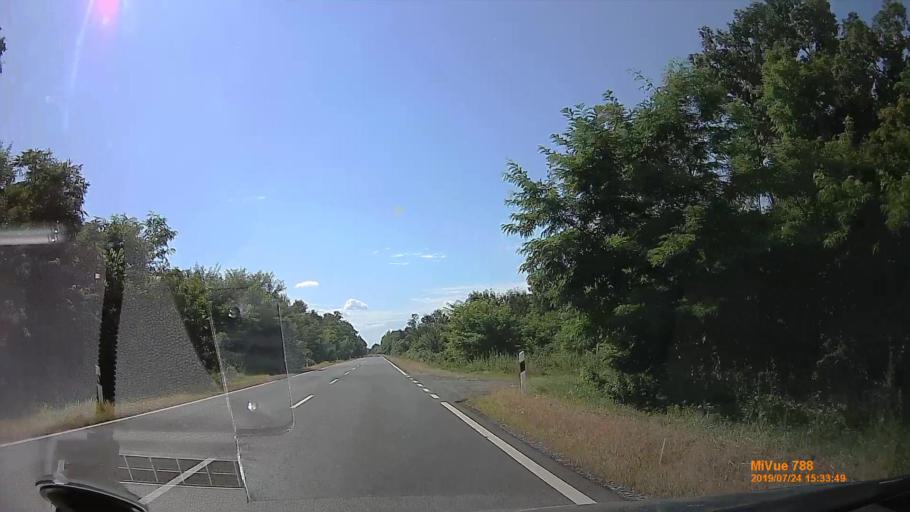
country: HU
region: Szabolcs-Szatmar-Bereg
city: Vasarosnameny
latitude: 48.1513
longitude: 22.3863
